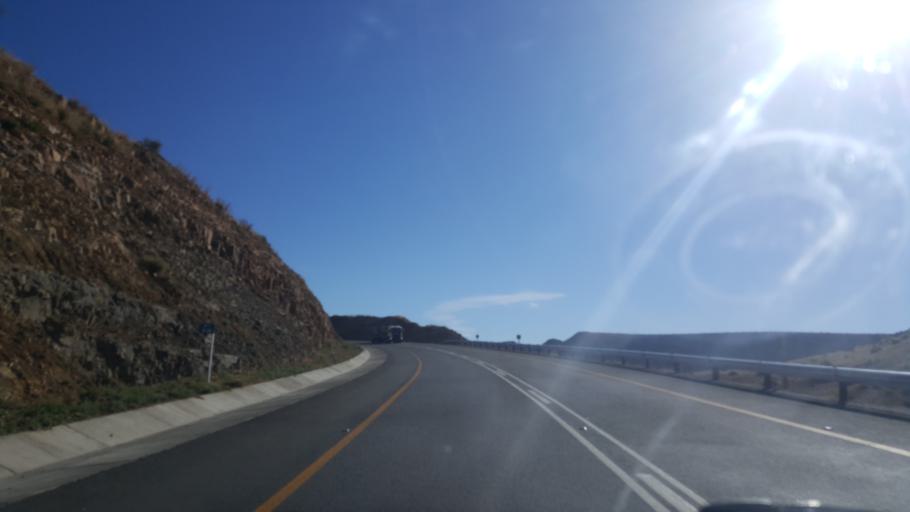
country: ZA
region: Eastern Cape
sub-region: Chris Hani District Municipality
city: Middelburg
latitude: -31.3811
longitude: 25.0336
